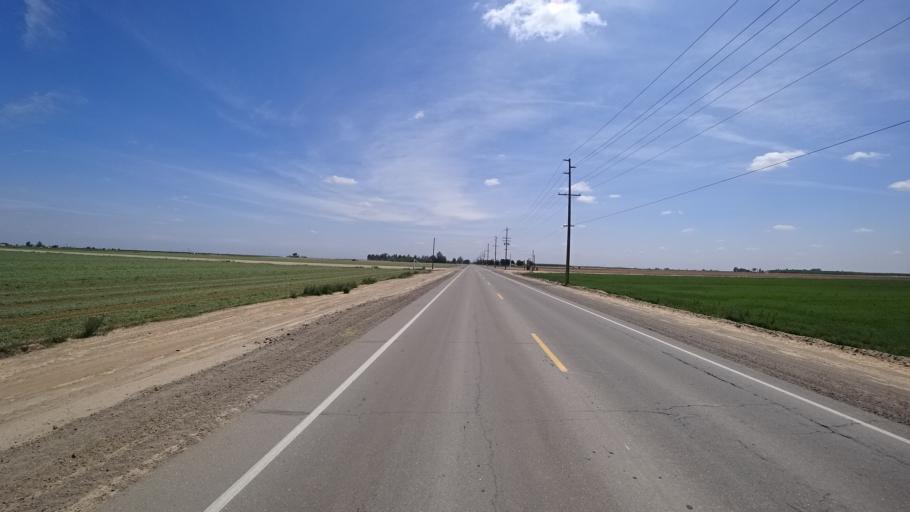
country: US
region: California
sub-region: Kings County
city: Home Garden
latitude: 36.2986
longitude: -119.5800
